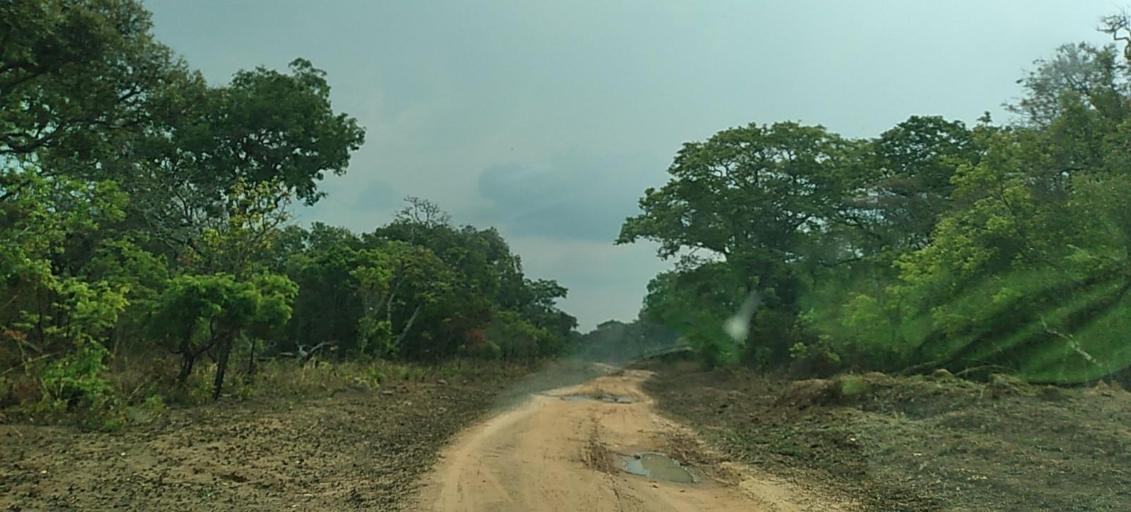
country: ZM
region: North-Western
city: Mwinilunga
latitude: -11.4694
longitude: 24.4649
